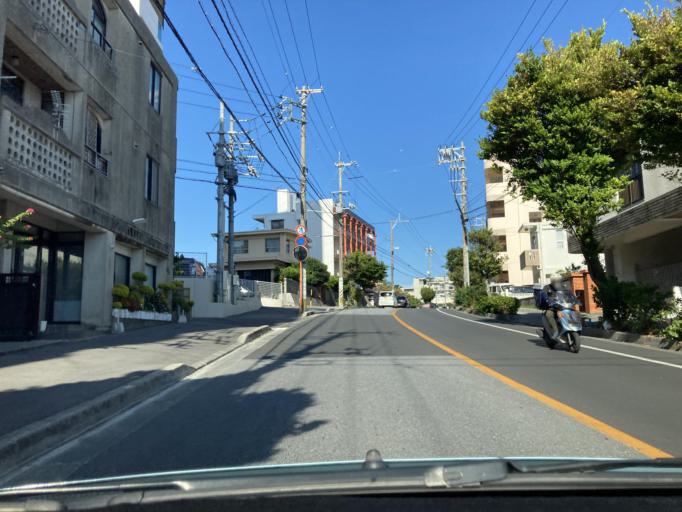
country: JP
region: Okinawa
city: Naha-shi
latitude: 26.2315
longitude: 127.7233
